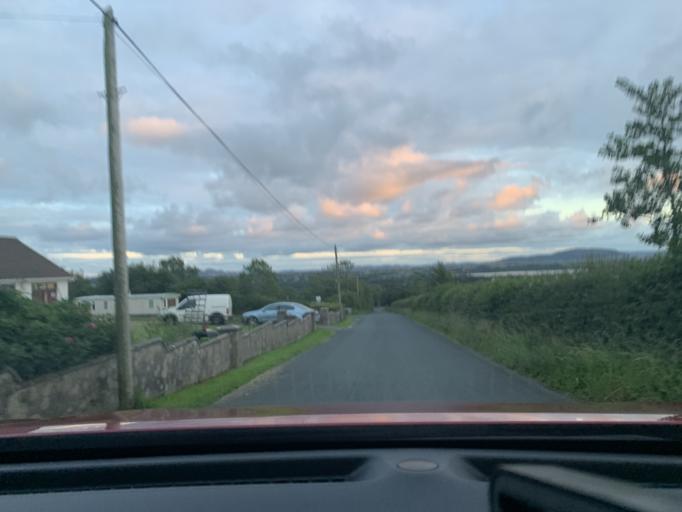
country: IE
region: Connaught
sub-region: Sligo
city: Sligo
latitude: 54.3501
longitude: -8.4887
